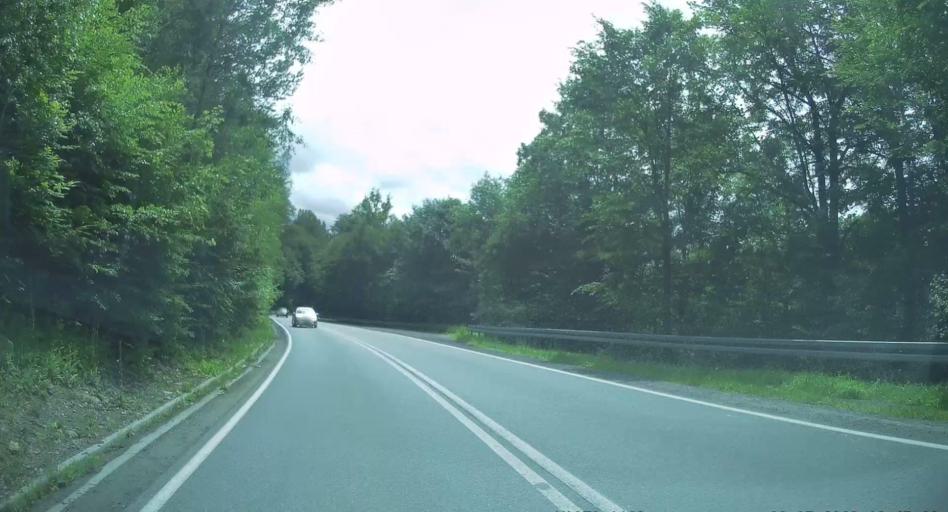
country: PL
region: Lesser Poland Voivodeship
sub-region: Powiat nowosadecki
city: Muszyna
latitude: 49.3500
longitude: 20.8026
